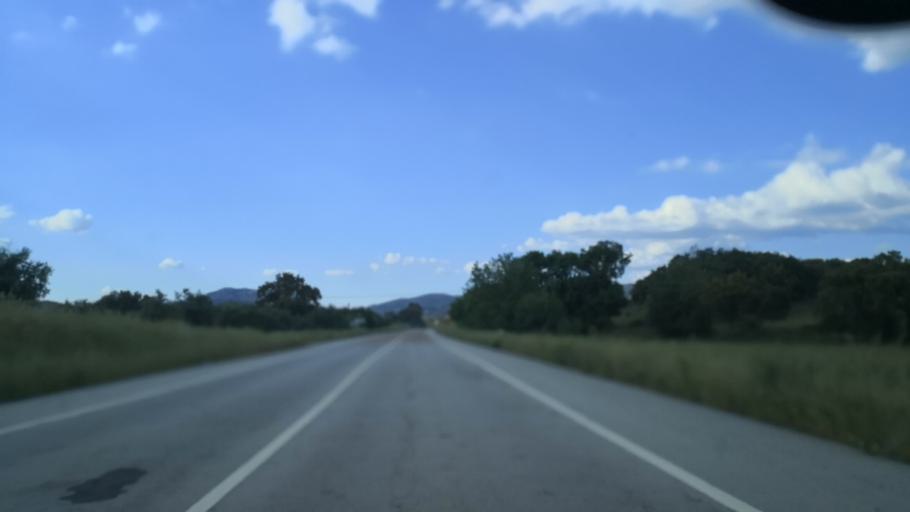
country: PT
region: Portalegre
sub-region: Portalegre
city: Portalegre
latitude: 39.2536
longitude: -7.4476
